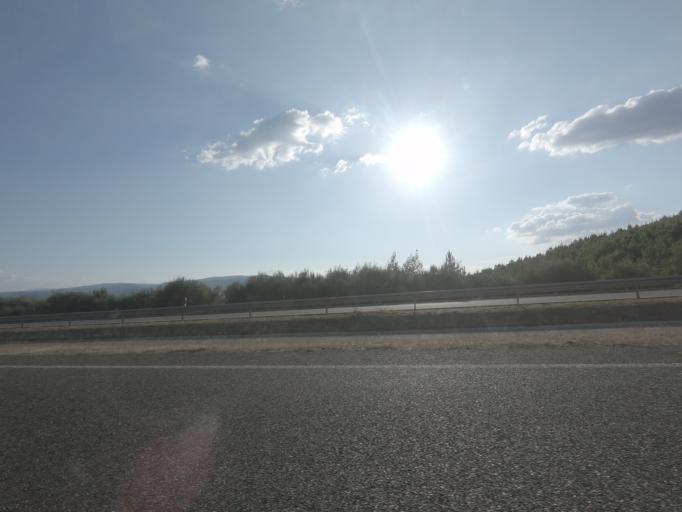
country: ES
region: Galicia
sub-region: Provincia de Ourense
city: Oimbra
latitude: 41.8849
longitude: -7.4271
